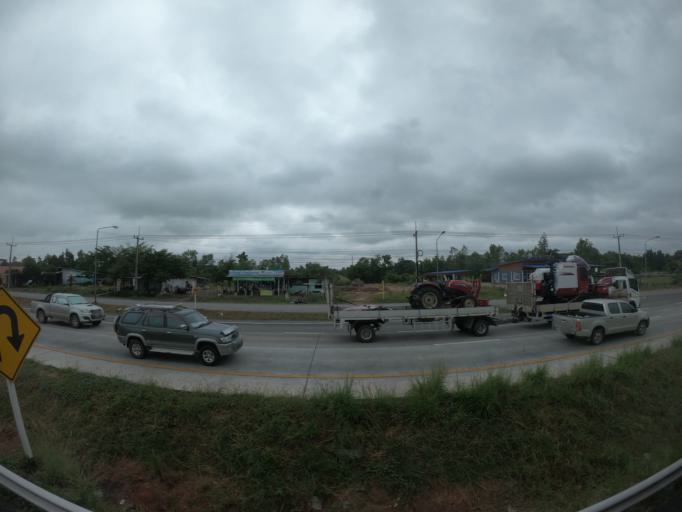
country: TH
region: Nakhon Ratchasima
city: Bua Lai
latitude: 15.6411
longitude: 102.5698
